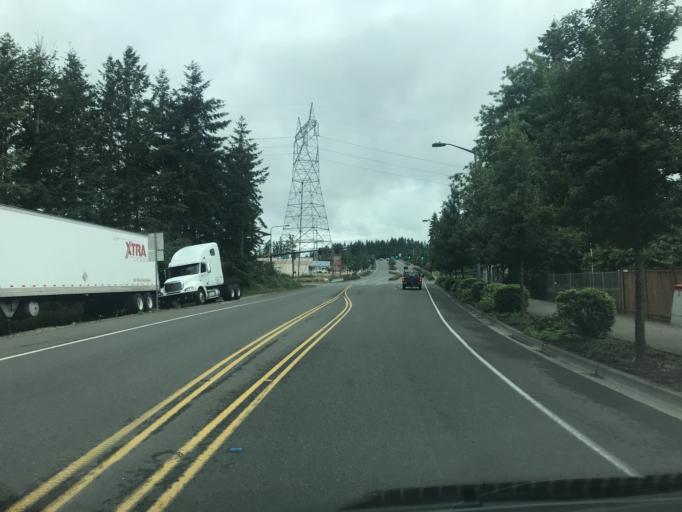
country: US
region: Washington
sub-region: King County
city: Covington
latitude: 47.3516
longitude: -122.1210
